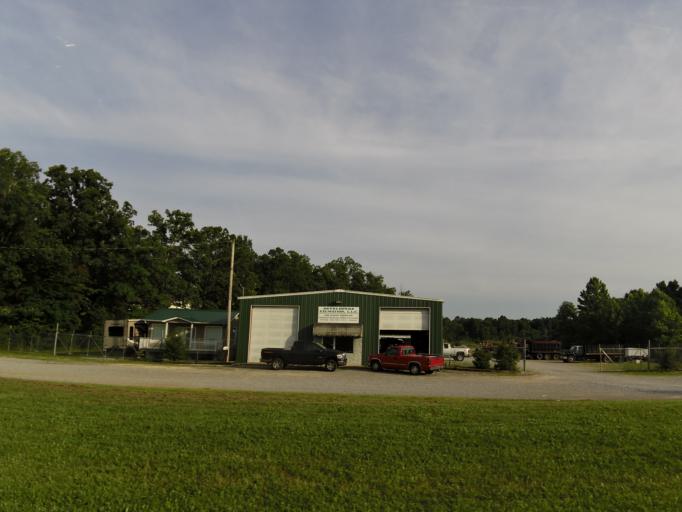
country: US
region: Tennessee
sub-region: Dickson County
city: Dickson
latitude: 36.0654
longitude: -87.3640
